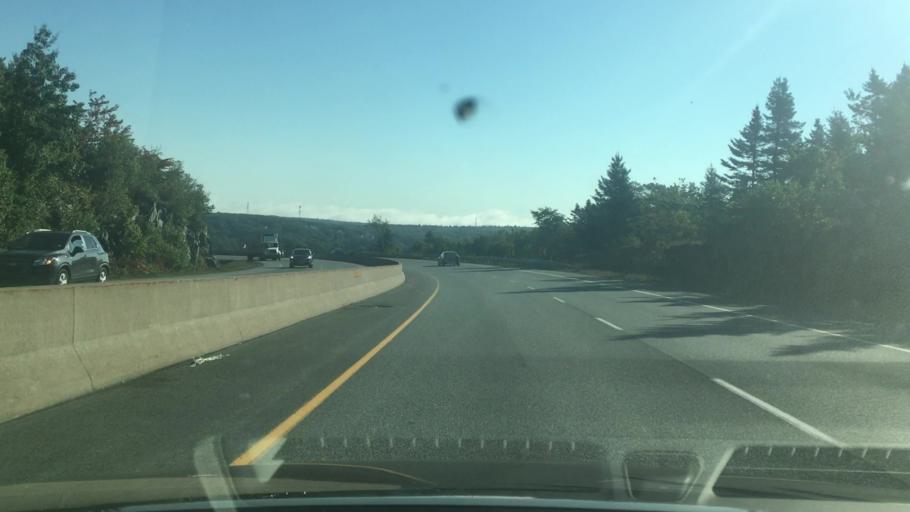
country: CA
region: Nova Scotia
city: Dartmouth
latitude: 44.7343
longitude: -63.6652
